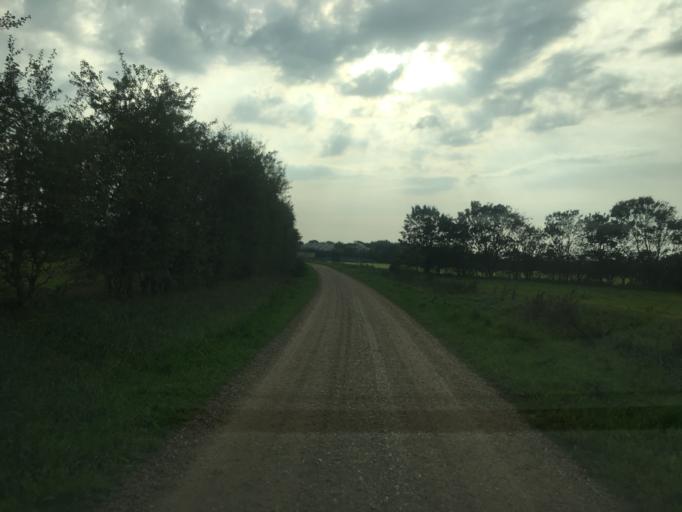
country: DK
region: South Denmark
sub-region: Tonder Kommune
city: Logumkloster
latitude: 54.9891
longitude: 9.0207
